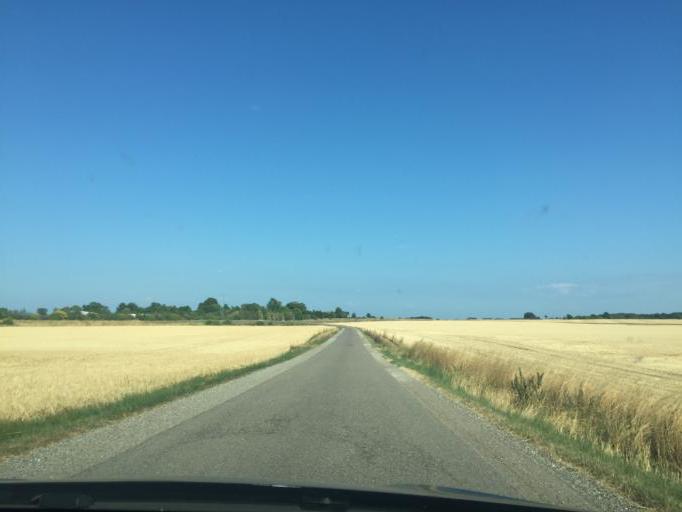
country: DK
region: Central Jutland
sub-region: Odder Kommune
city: Odder
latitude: 55.9303
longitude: 10.2281
